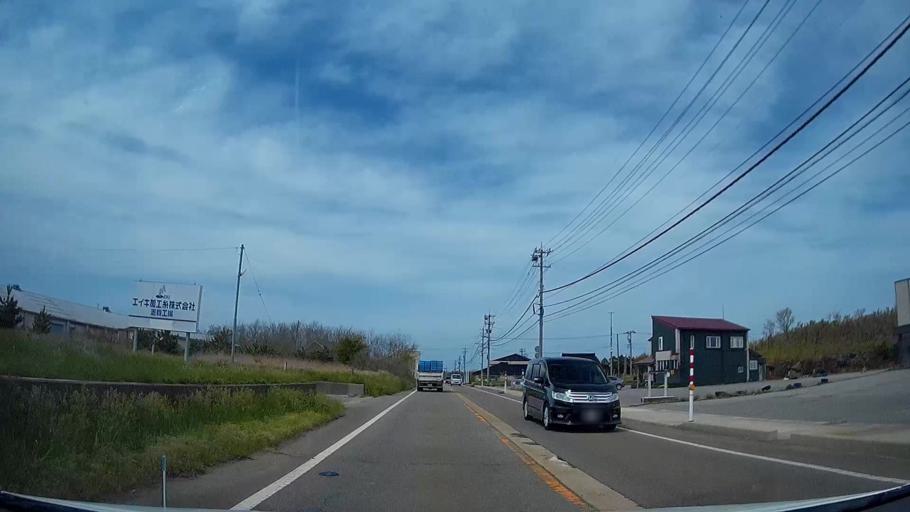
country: JP
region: Ishikawa
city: Hakui
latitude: 36.9896
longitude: 136.7763
